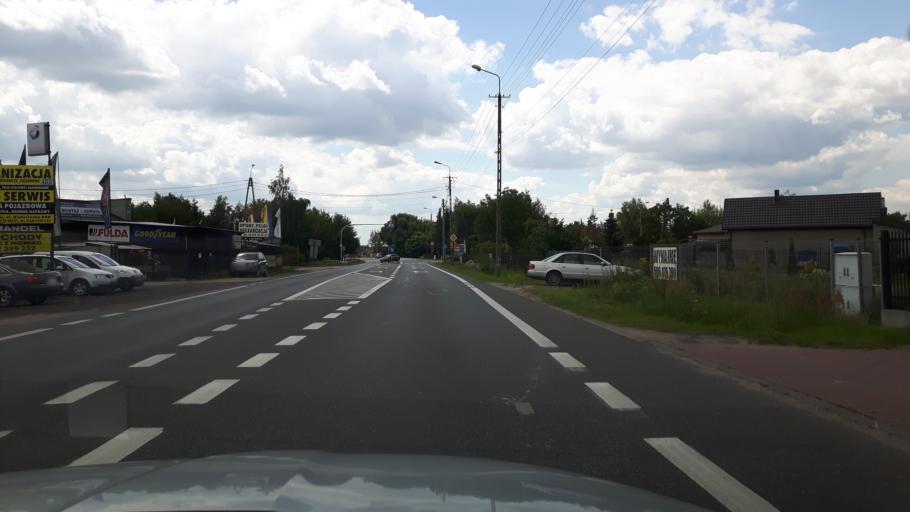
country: PL
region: Masovian Voivodeship
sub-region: Powiat wyszkowski
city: Wyszkow
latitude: 52.6125
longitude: 21.4772
